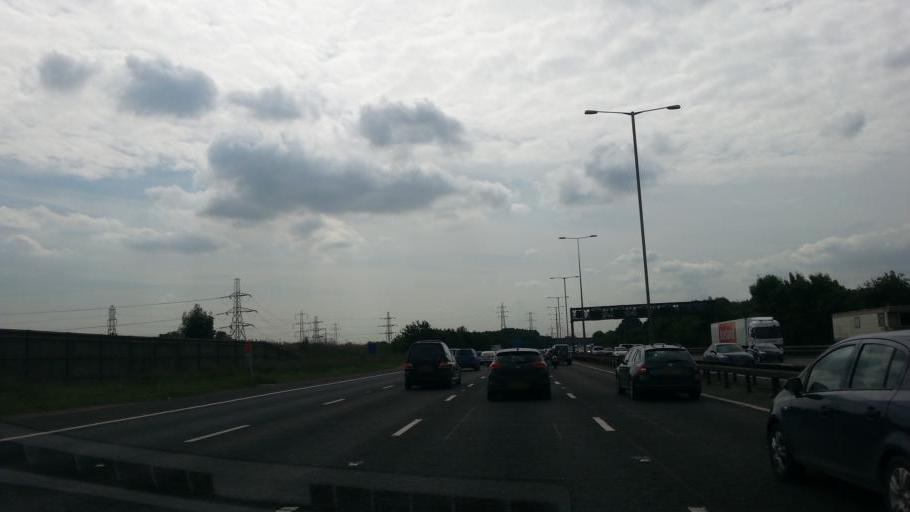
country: GB
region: England
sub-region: Greater London
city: Uxbridge
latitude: 51.5287
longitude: -0.4985
